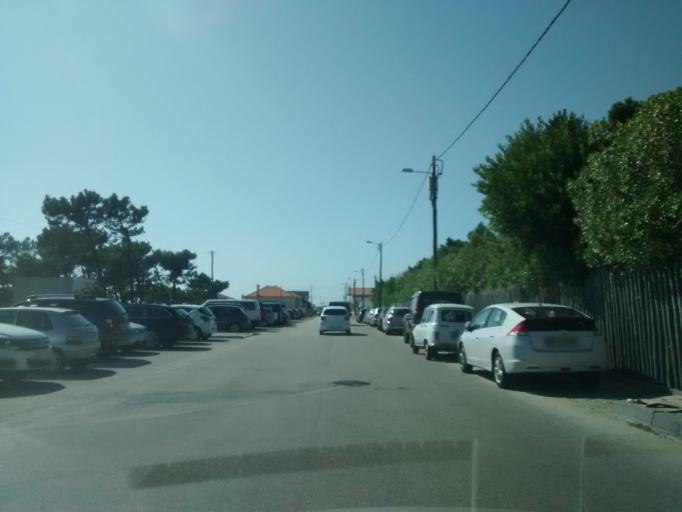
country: PT
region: Aveiro
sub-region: Ilhavo
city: Gafanha da Nazare
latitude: 40.6673
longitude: -8.7390
